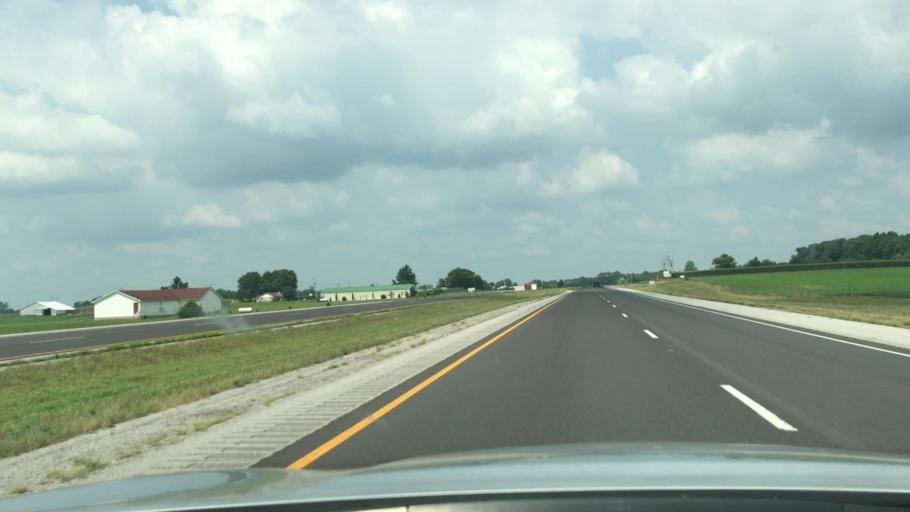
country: US
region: Kentucky
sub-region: Todd County
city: Elkton
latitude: 36.8029
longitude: -87.0910
